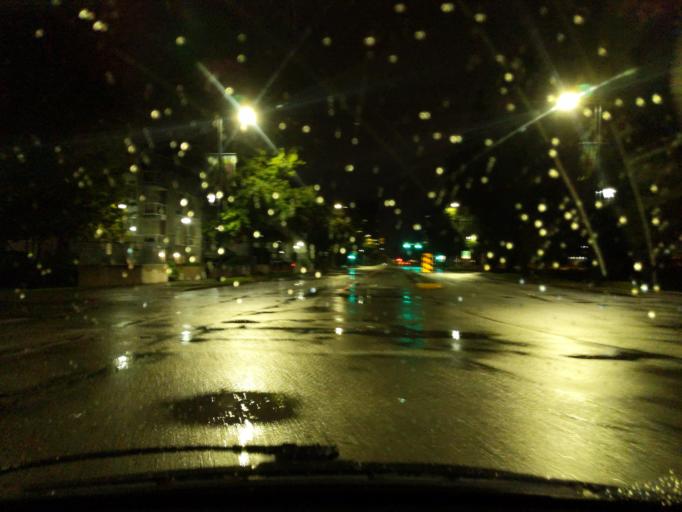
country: CA
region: British Columbia
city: New Westminster
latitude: 49.1930
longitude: -122.8509
